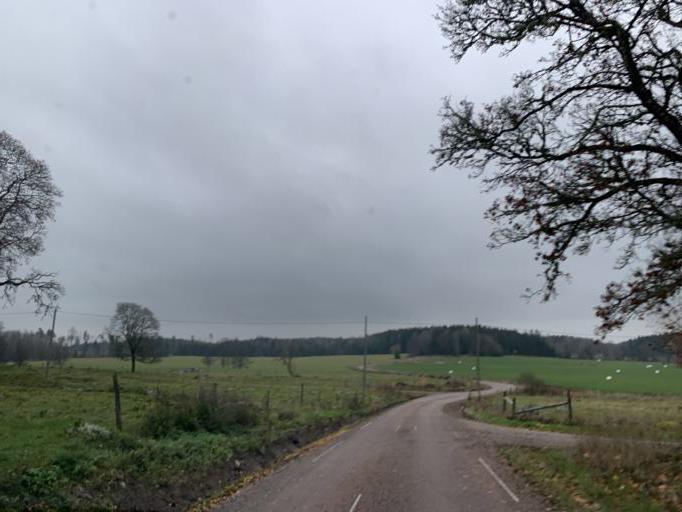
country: SE
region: Vaestmanland
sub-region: Surahammars Kommun
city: Surahammar
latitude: 59.6528
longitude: 16.0739
